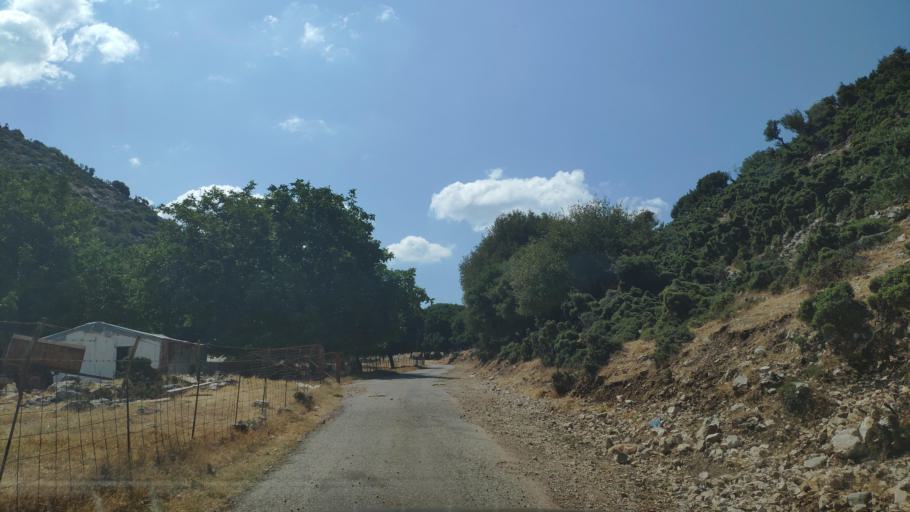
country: GR
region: West Greece
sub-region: Nomos Aitolias kai Akarnanias
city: Monastirakion
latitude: 38.8048
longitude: 20.9461
